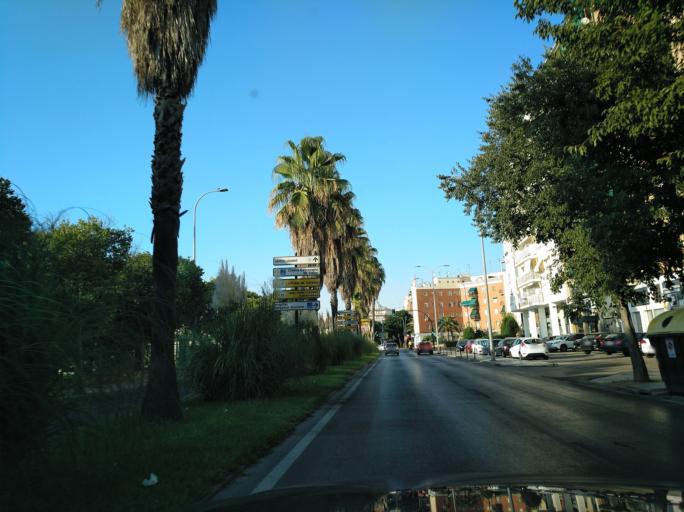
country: ES
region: Extremadura
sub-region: Provincia de Badajoz
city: Badajoz
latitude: 38.8697
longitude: -6.9791
